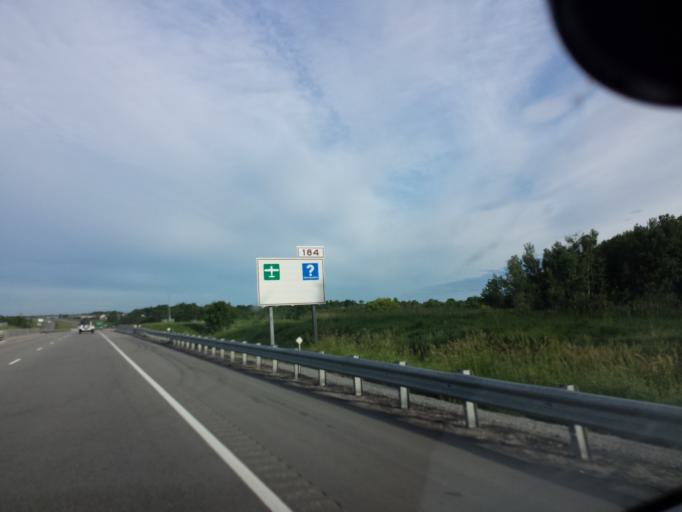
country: CA
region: Ontario
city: Arnprior
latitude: 45.4200
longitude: -76.3428
